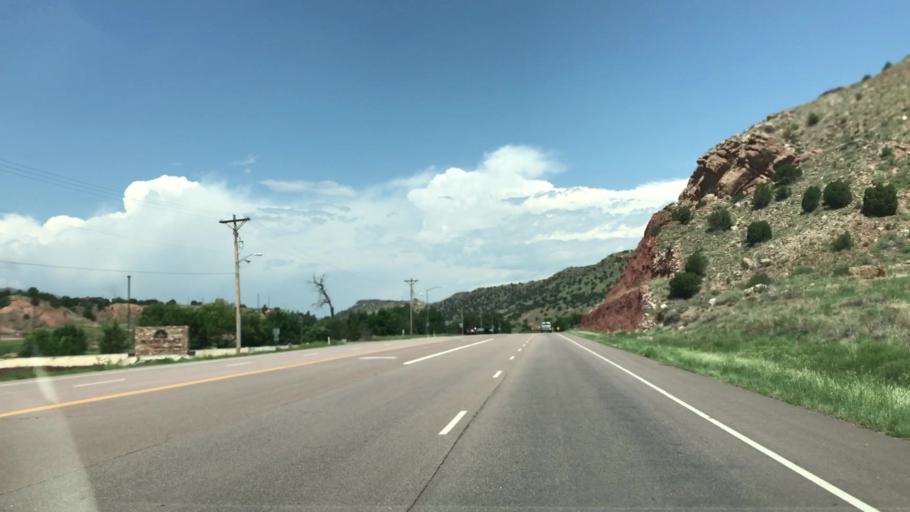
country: US
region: Colorado
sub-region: Fremont County
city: Canon City
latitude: 38.4399
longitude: -105.2534
